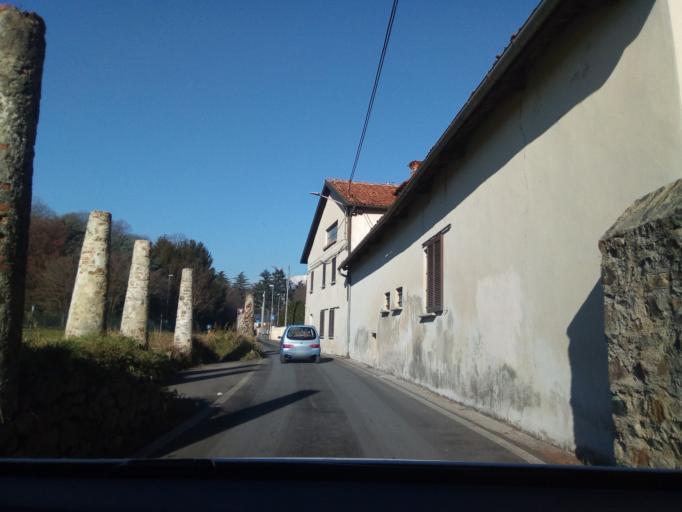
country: IT
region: Piedmont
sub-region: Provincia di Torino
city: Cascinette d'Ivrea
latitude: 45.4739
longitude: 7.8916
